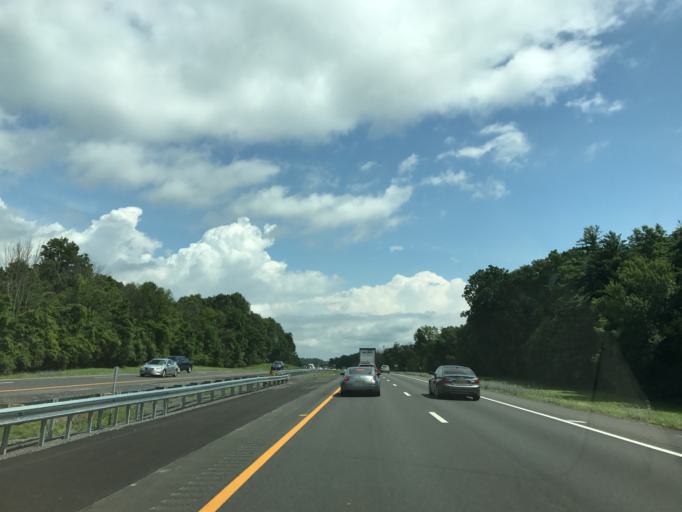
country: US
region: New York
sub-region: Ulster County
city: Saugerties
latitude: 42.1297
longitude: -73.9533
